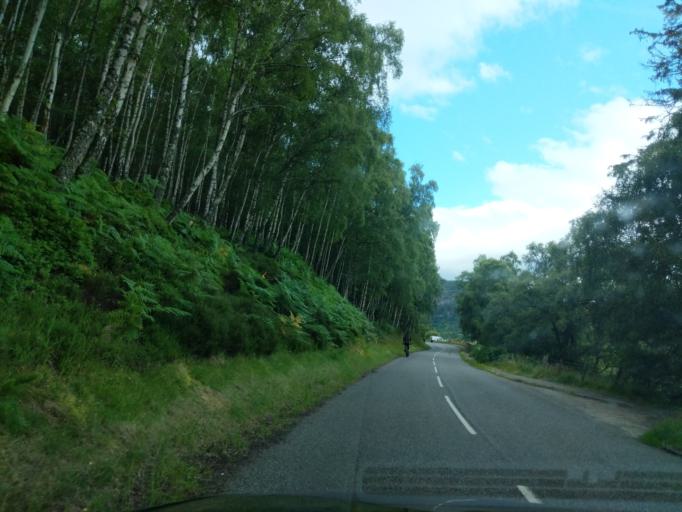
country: GB
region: Scotland
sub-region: Aberdeenshire
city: Ballater
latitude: 57.0551
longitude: -3.0144
